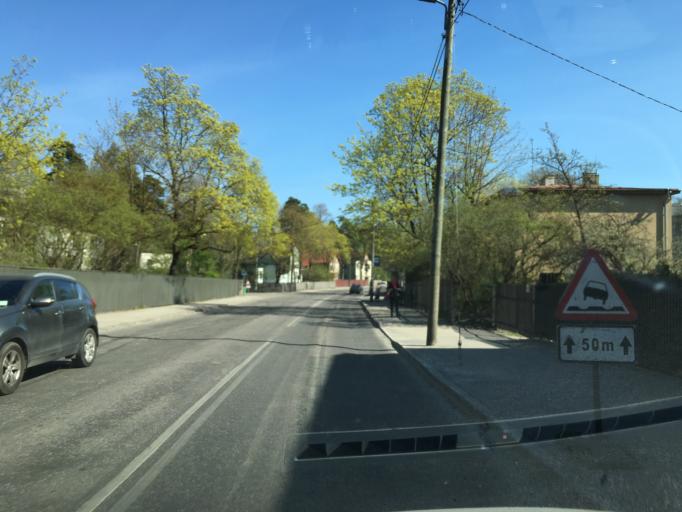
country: EE
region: Harju
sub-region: Saue vald
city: Laagri
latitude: 59.3877
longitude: 24.6860
